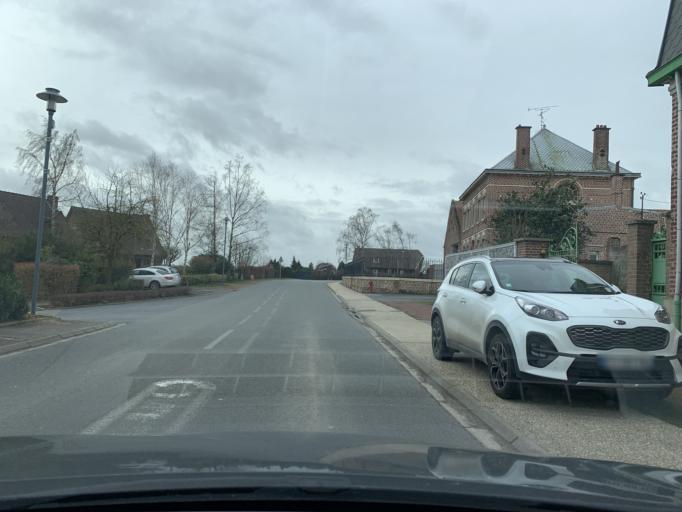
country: FR
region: Nord-Pas-de-Calais
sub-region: Departement du Nord
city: Cambrai
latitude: 50.1536
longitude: 3.2791
